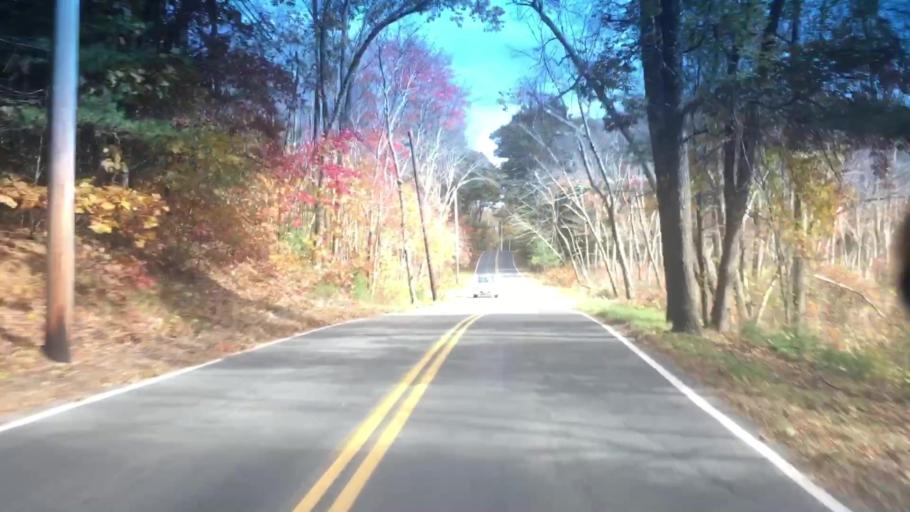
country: US
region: Massachusetts
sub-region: Norfolk County
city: Dover
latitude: 42.2093
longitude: -71.2714
